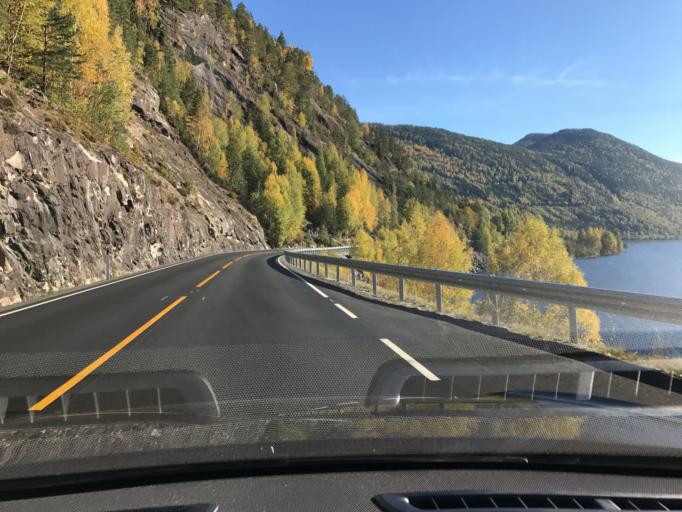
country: NO
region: Buskerud
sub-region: Krodsherad
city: Noresund
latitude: 60.3298
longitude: 9.6546
